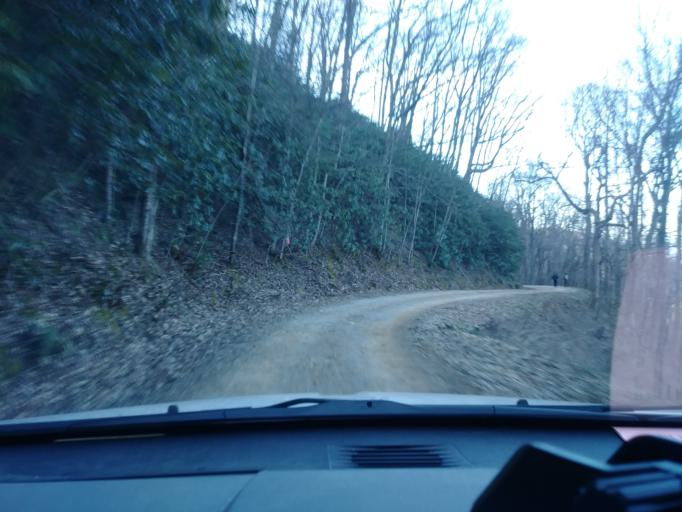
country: US
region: Tennessee
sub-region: Greene County
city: Tusculum
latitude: 36.0663
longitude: -82.6811
